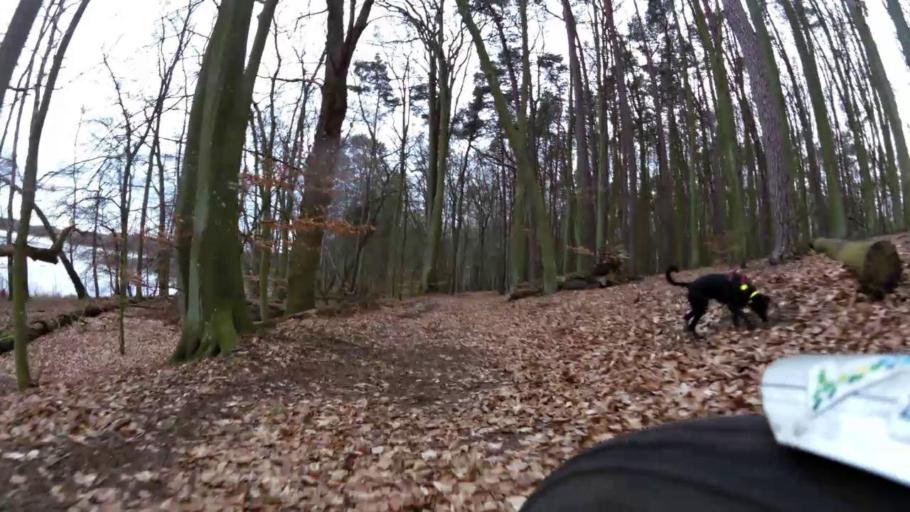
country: PL
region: West Pomeranian Voivodeship
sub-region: Powiat kamienski
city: Miedzyzdroje
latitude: 53.9413
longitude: 14.5580
